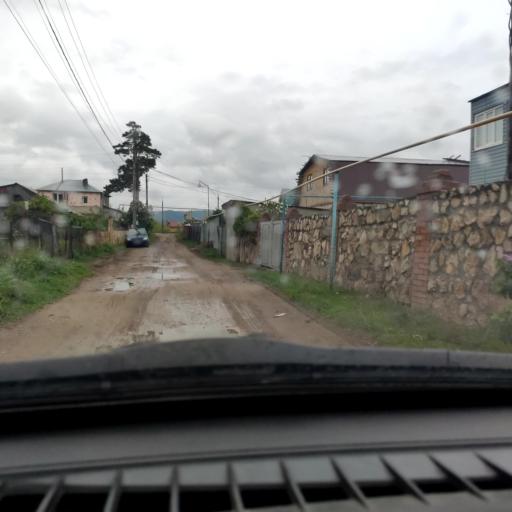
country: RU
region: Samara
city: Zhigulevsk
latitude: 53.4660
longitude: 49.5978
